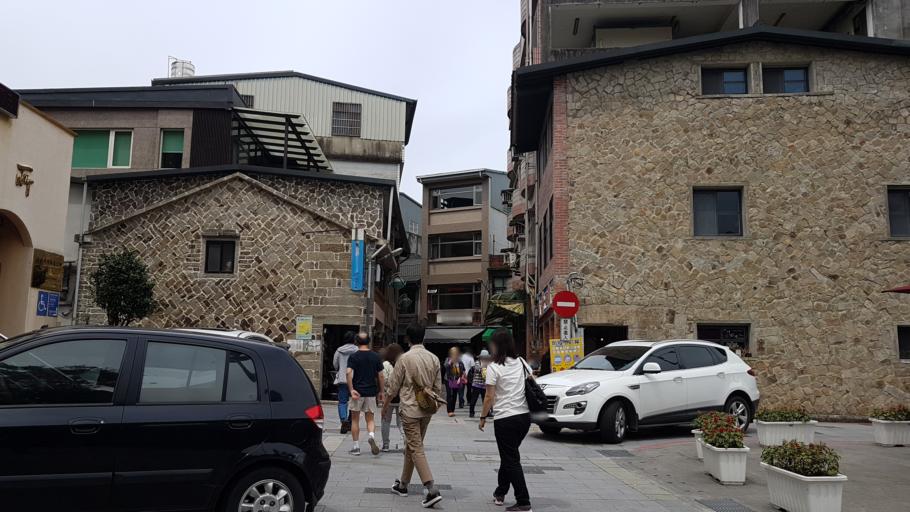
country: TW
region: Taiwan
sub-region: Yilan
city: Yilan
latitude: 24.9361
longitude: 121.7118
